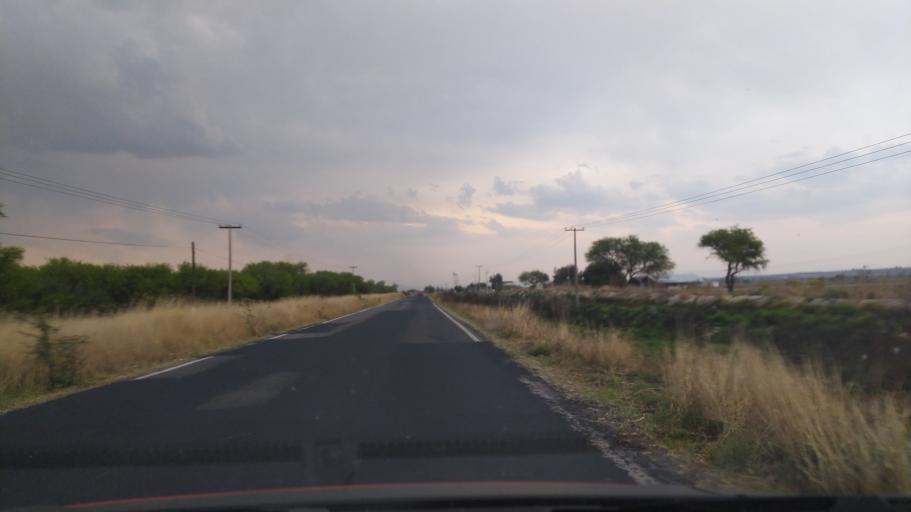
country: MX
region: Guanajuato
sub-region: San Francisco del Rincon
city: San Ignacio de Hidalgo
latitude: 20.8407
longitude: -101.8976
